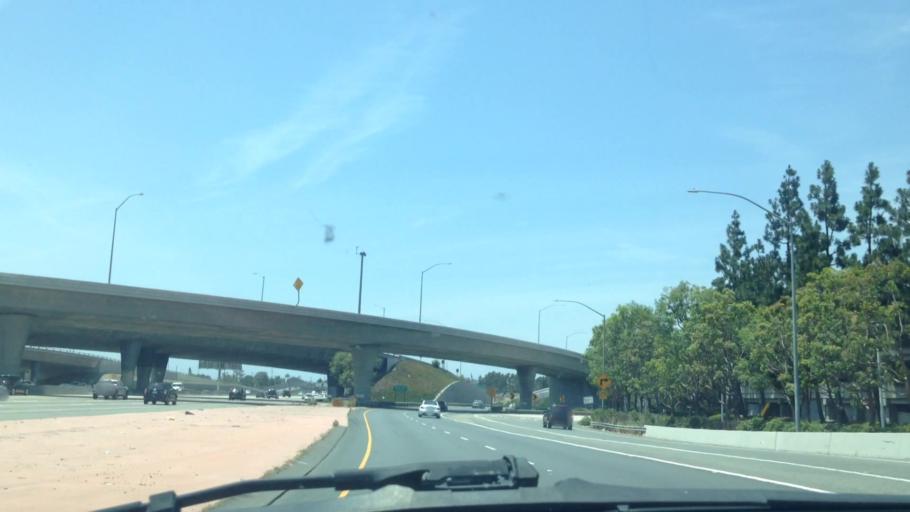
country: US
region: California
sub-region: Orange County
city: Costa Mesa
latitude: 33.6879
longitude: -117.8974
